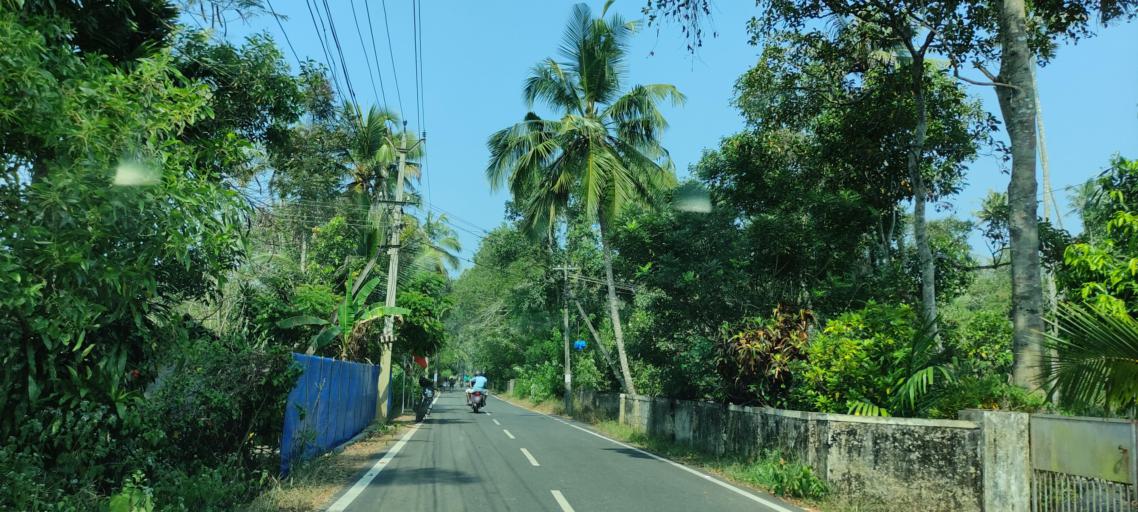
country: IN
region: Kerala
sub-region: Alappuzha
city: Shertallai
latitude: 9.5979
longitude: 76.3117
